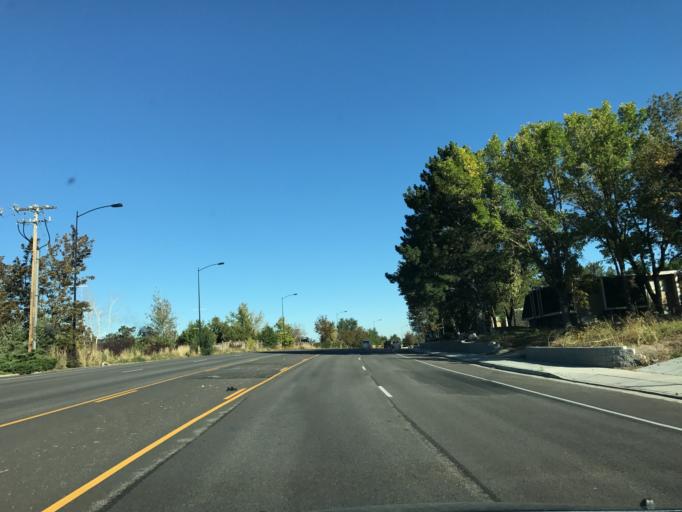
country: US
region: Utah
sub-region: Weber County
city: Washington Terrace
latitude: 41.1725
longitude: -111.9485
